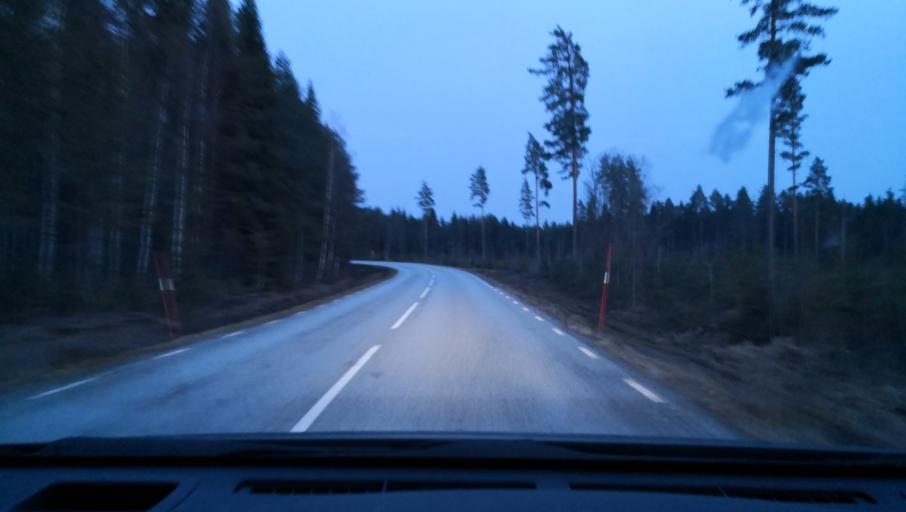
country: SE
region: OErebro
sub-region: Lindesbergs Kommun
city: Frovi
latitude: 59.5928
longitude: 15.3910
